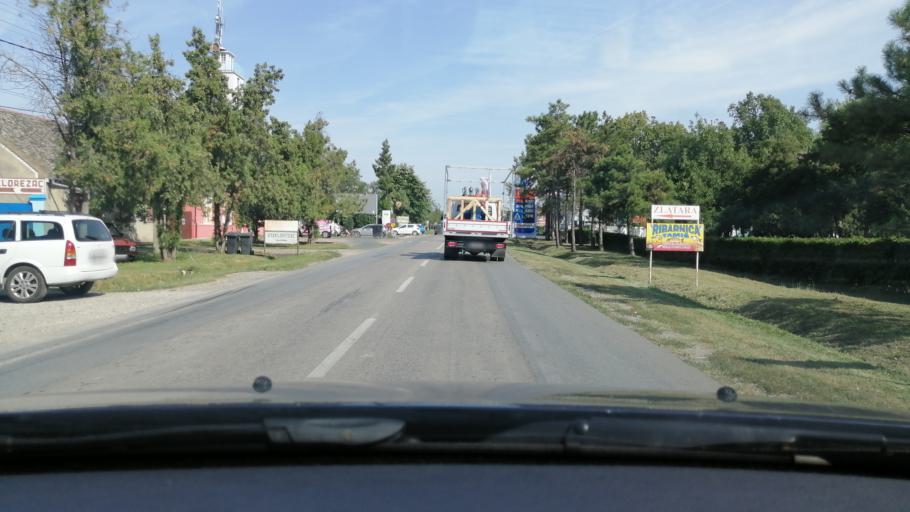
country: RS
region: Autonomna Pokrajina Vojvodina
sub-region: Juznobanatski Okrug
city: Kovacica
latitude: 45.1124
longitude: 20.6183
